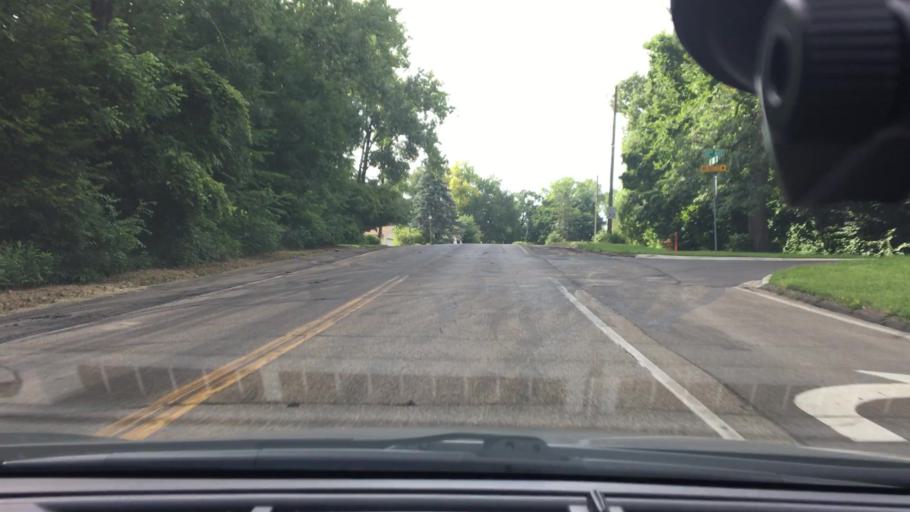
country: US
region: Minnesota
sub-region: Hennepin County
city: Plymouth
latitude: 45.0132
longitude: -93.4378
